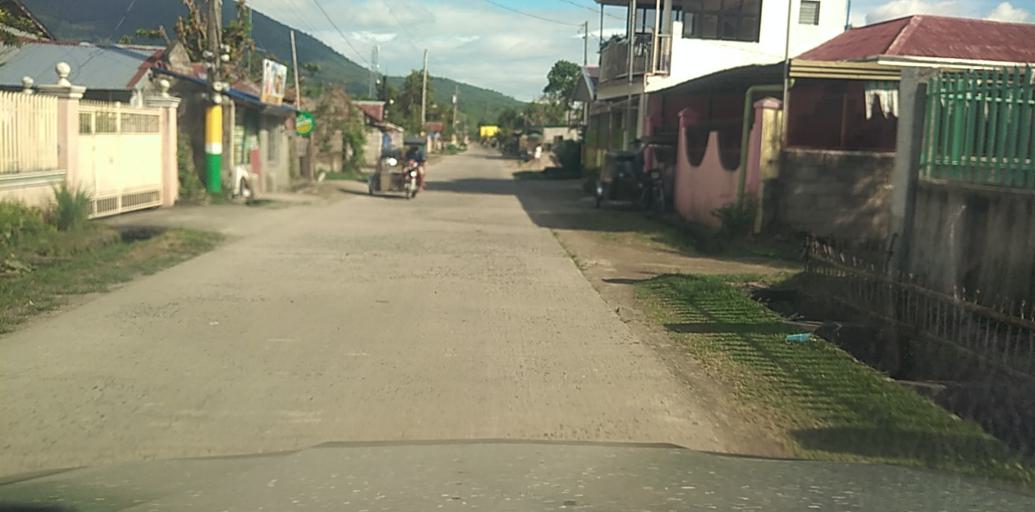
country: PH
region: Central Luzon
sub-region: Province of Pampanga
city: Buensuseso
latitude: 15.1919
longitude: 120.6863
